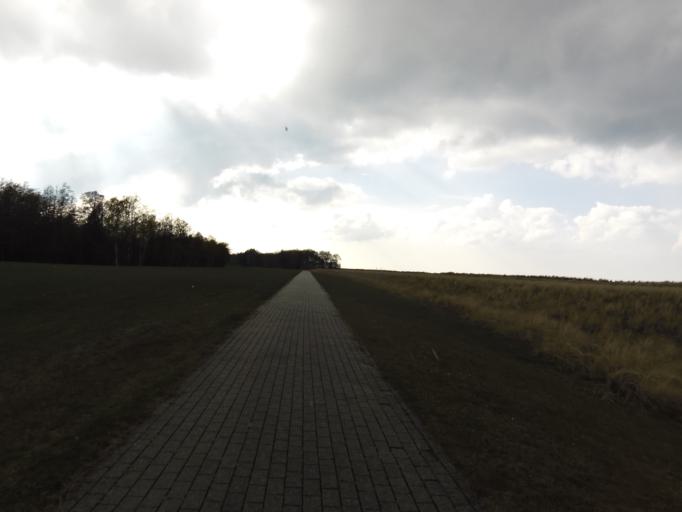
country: DE
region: Mecklenburg-Vorpommern
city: Zingst
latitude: 54.4406
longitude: 12.7737
